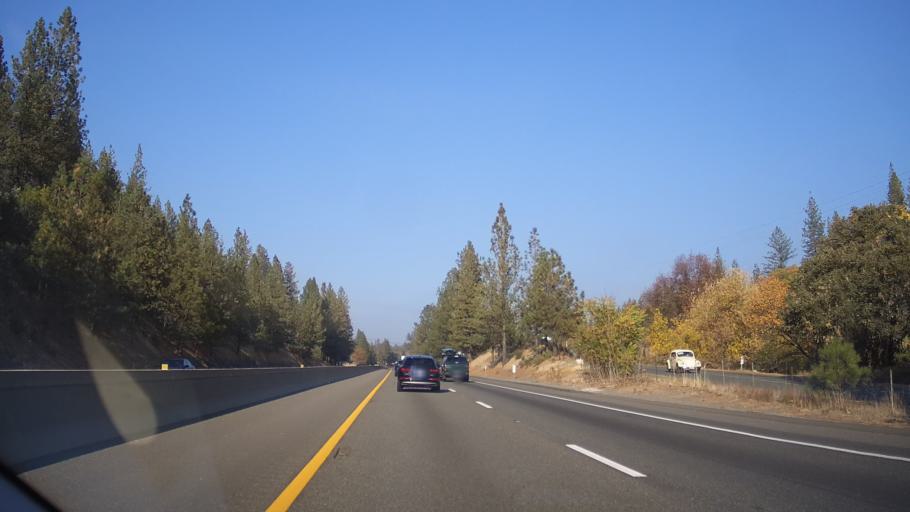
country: US
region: California
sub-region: Placer County
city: Colfax
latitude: 39.0805
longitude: -120.9588
